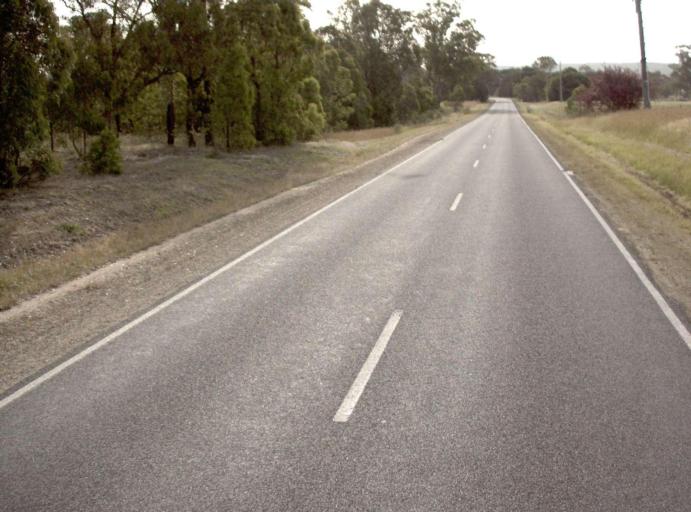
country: AU
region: Victoria
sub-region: Wellington
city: Heyfield
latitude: -38.0596
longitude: 146.6421
